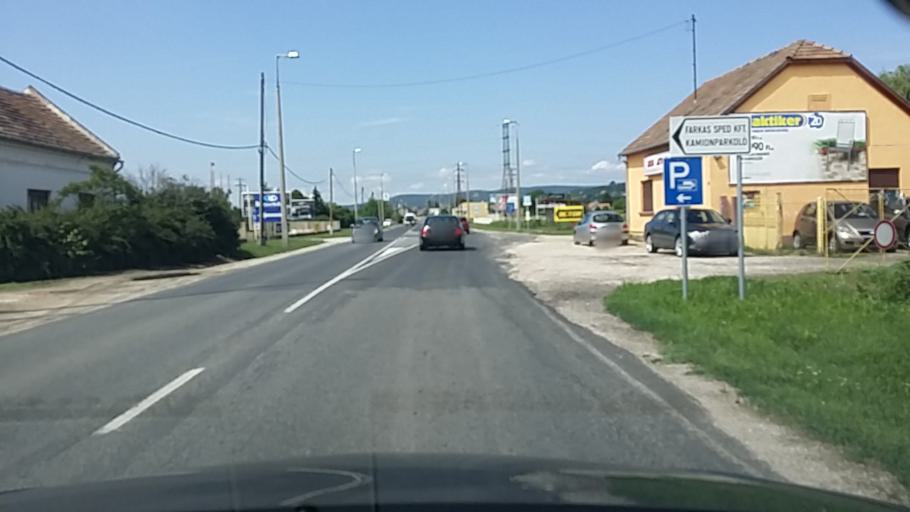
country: HU
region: Komarom-Esztergom
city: Esztergom
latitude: 47.7710
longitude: 18.7377
